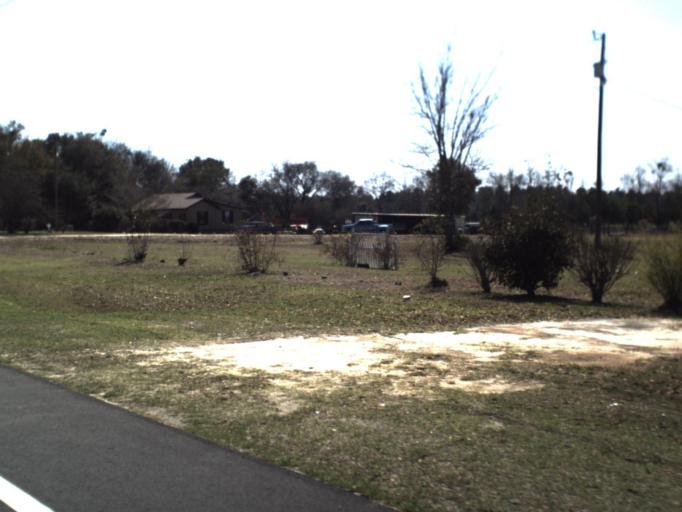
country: US
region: Florida
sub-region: Jackson County
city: Malone
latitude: 30.8459
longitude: -85.0699
